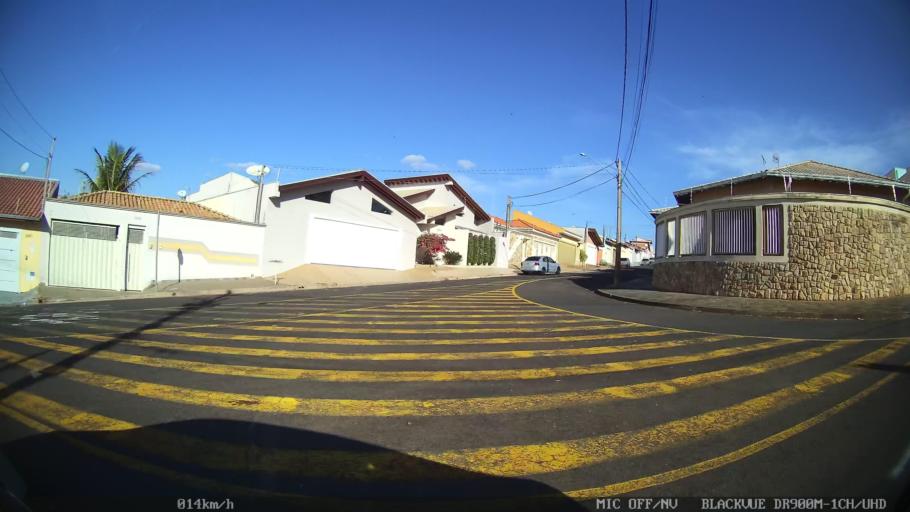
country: BR
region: Sao Paulo
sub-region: Franca
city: Franca
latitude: -20.5238
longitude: -47.4166
